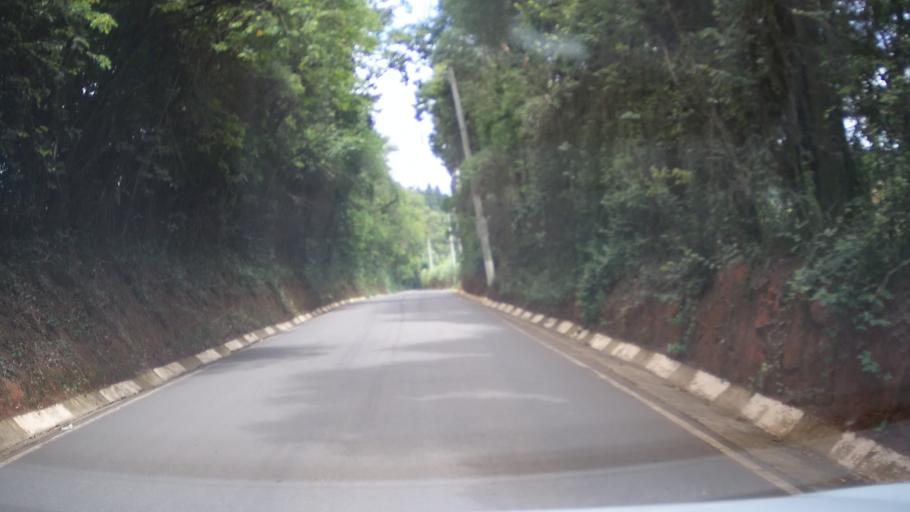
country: BR
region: Sao Paulo
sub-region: Vinhedo
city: Vinhedo
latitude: -23.0785
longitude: -47.0280
